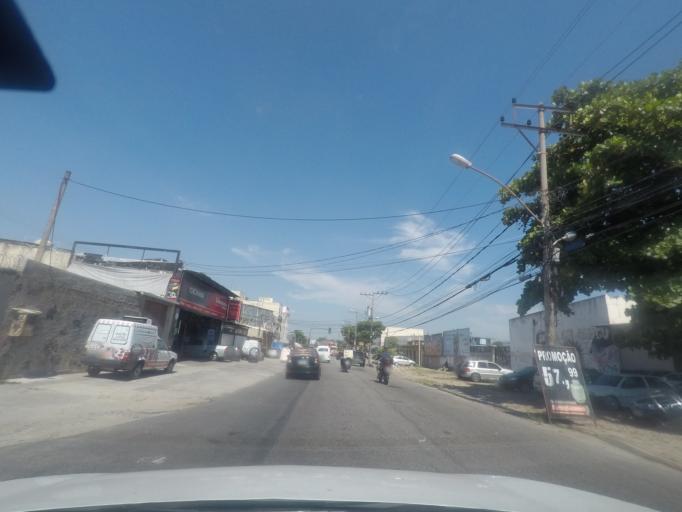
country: BR
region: Rio de Janeiro
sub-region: Nilopolis
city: Nilopolis
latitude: -22.8795
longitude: -43.4537
